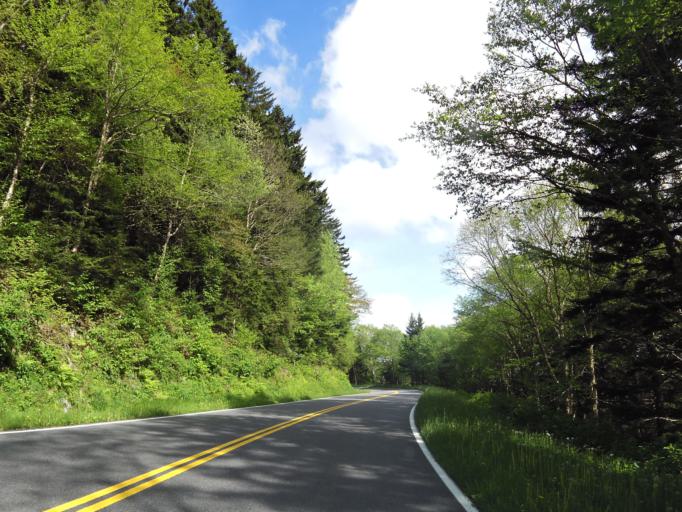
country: US
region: Tennessee
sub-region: Sevier County
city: Gatlinburg
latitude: 35.6104
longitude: -83.4424
